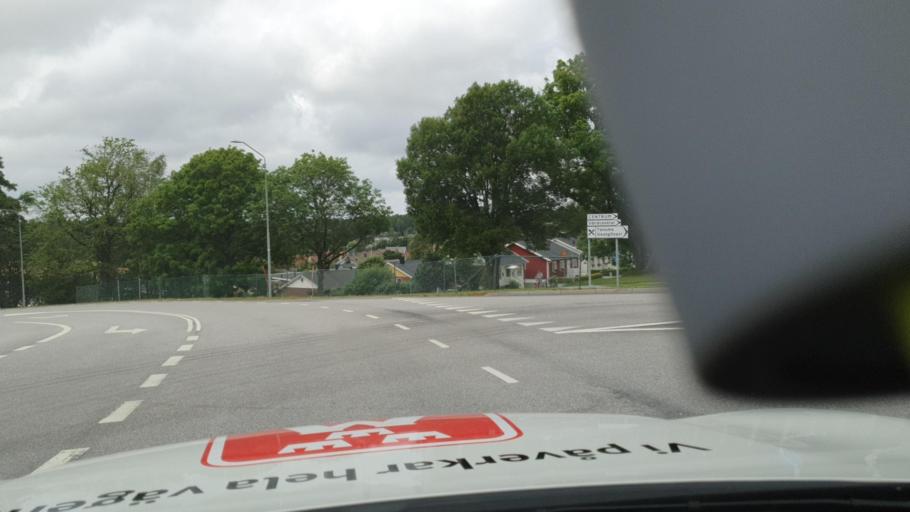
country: SE
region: Vaestra Goetaland
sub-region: Tanums Kommun
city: Tanumshede
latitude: 58.7228
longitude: 11.3221
